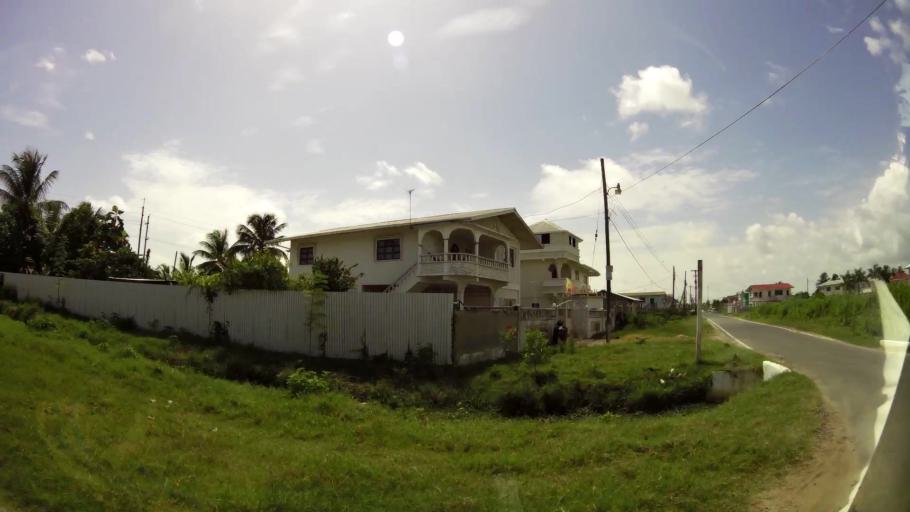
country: GY
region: Demerara-Mahaica
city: Mahaica Village
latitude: 6.7738
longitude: -58.0099
